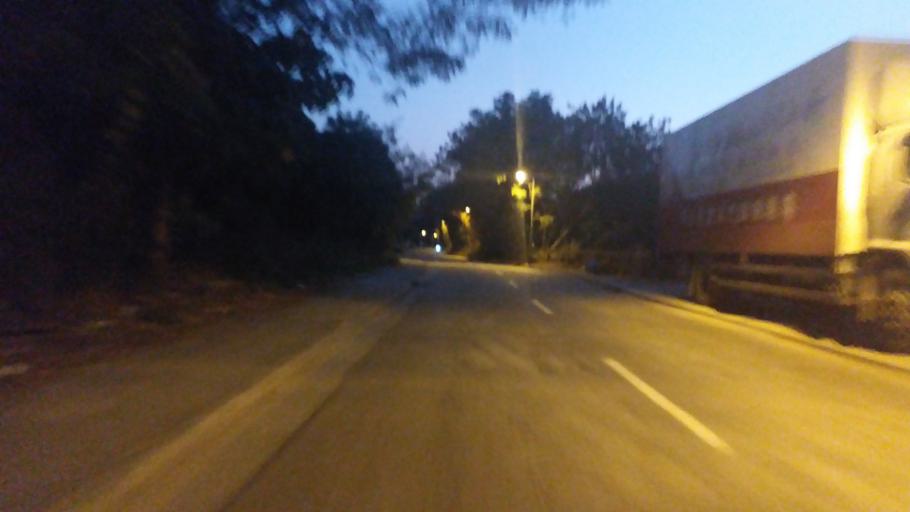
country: HK
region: Yuen Long
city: Yuen Long Kau Hui
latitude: 22.4453
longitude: 113.9972
